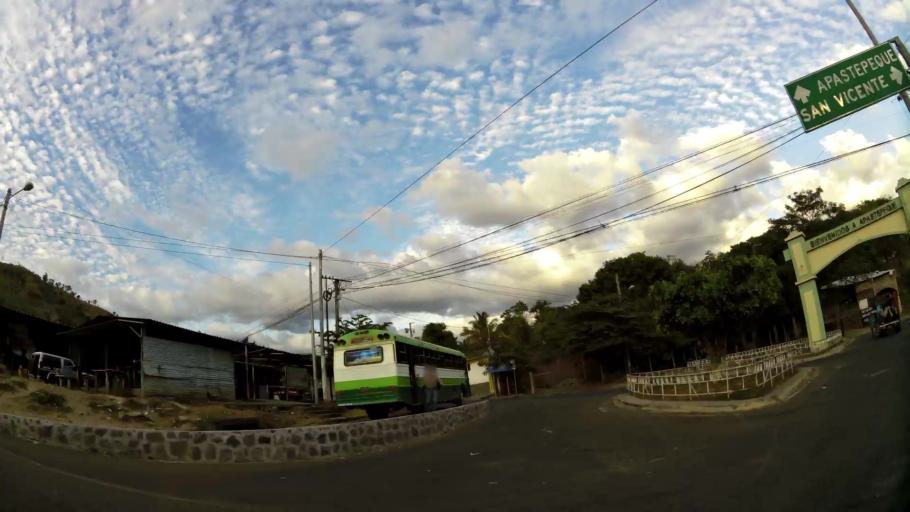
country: SV
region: San Vicente
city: Apastepeque
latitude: 13.6689
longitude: -88.7956
